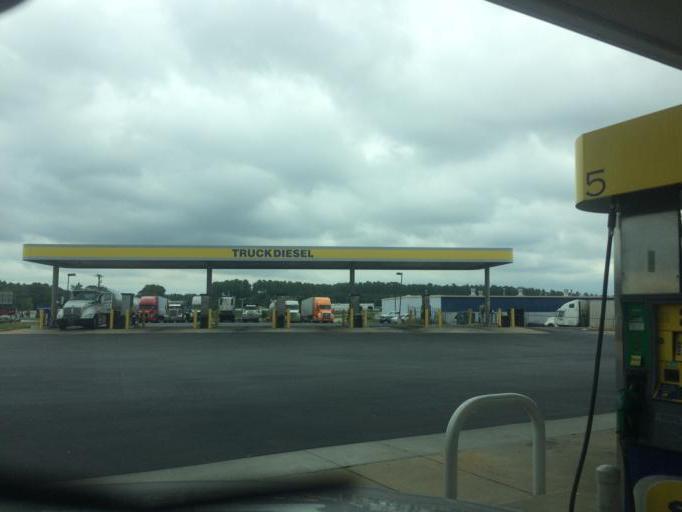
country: US
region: South Carolina
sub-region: Greenville County
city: Greer
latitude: 34.8737
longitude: -82.2247
